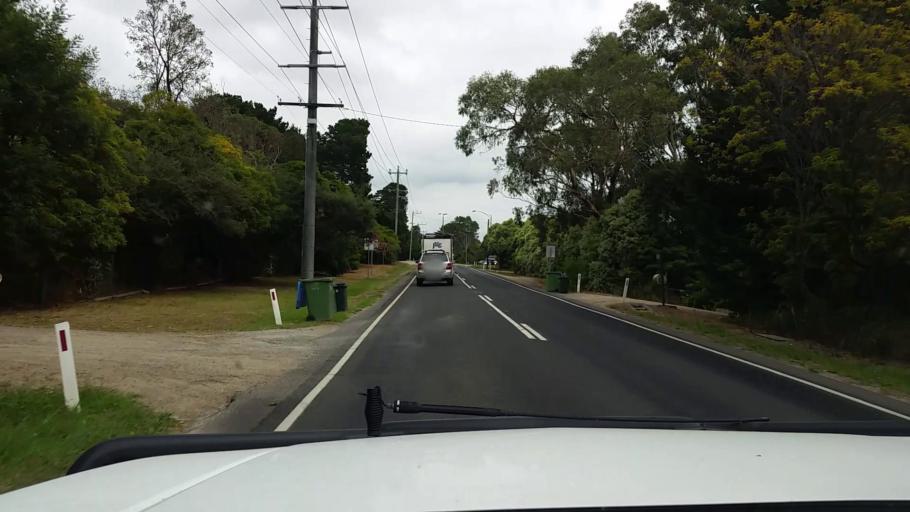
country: AU
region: Victoria
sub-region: Mornington Peninsula
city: Hastings
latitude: -38.2846
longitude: 145.1477
